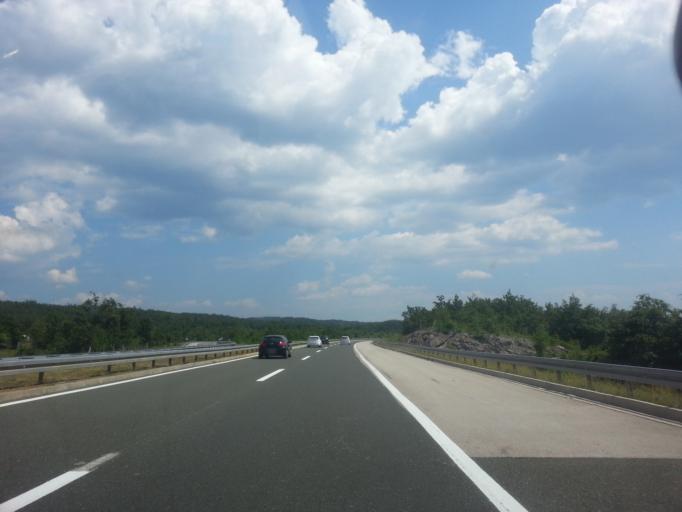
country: HR
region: Primorsko-Goranska
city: Matulji
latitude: 45.4283
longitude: 14.2927
